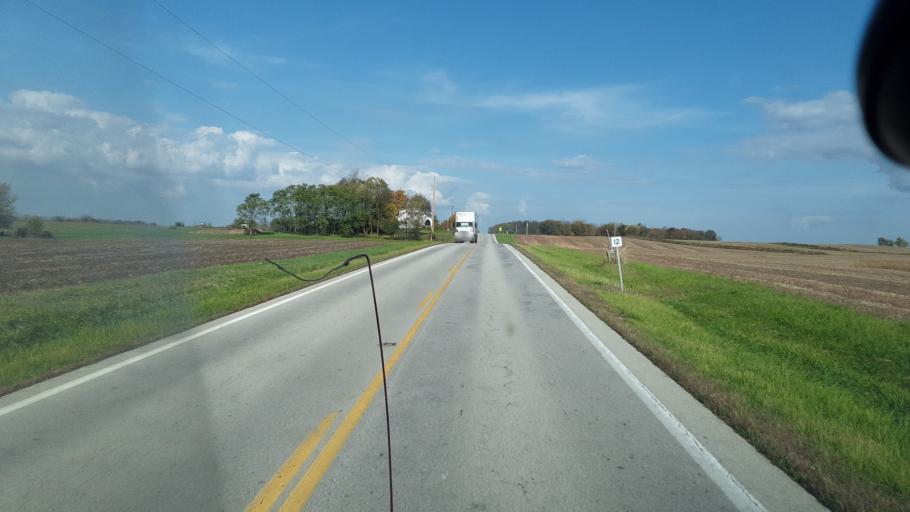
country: US
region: Ohio
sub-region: Clinton County
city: Sabina
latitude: 39.5271
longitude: -83.6995
